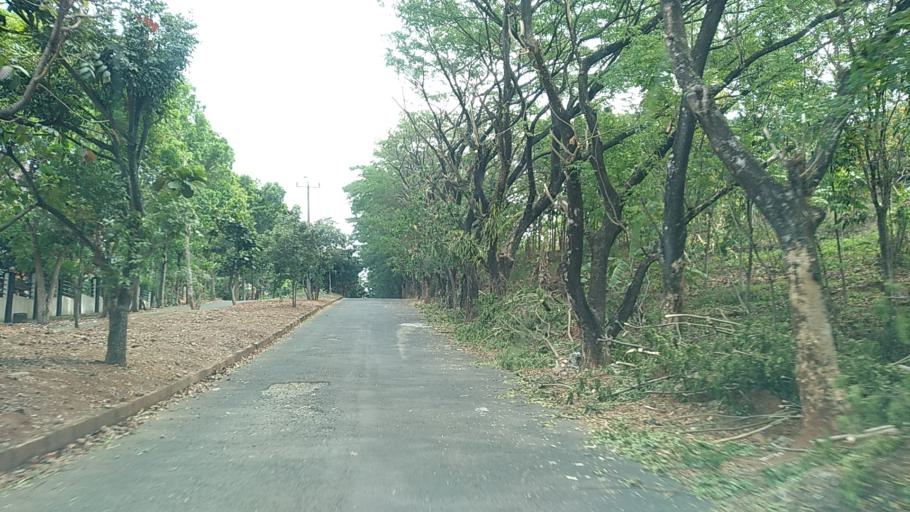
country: ID
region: Central Java
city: Semarang
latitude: -7.0494
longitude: 110.4362
